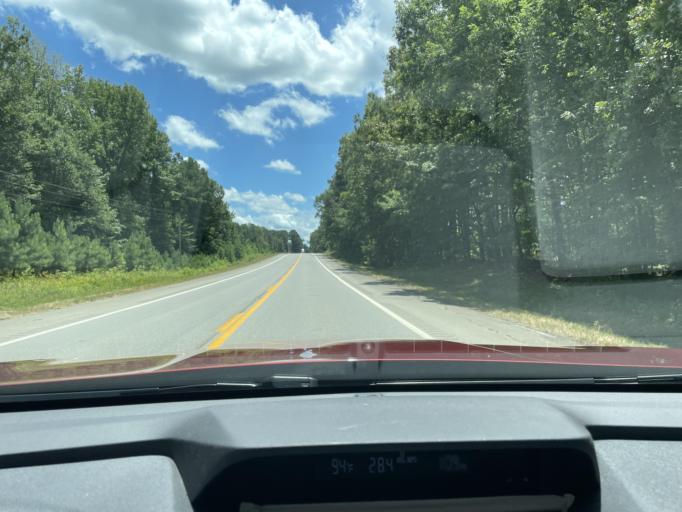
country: US
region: Arkansas
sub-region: Drew County
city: Monticello
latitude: 33.7345
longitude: -91.8166
